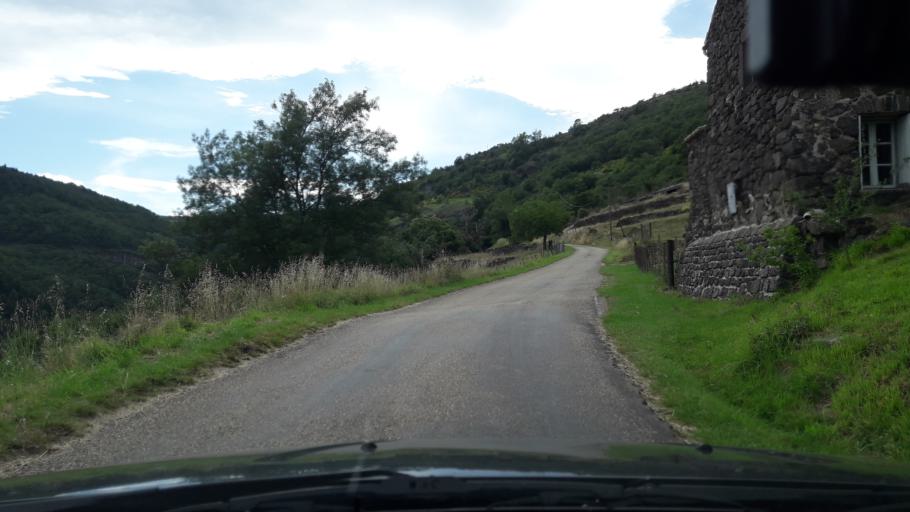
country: FR
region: Rhone-Alpes
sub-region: Departement de l'Ardeche
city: Alissas
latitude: 44.6801
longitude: 4.5945
